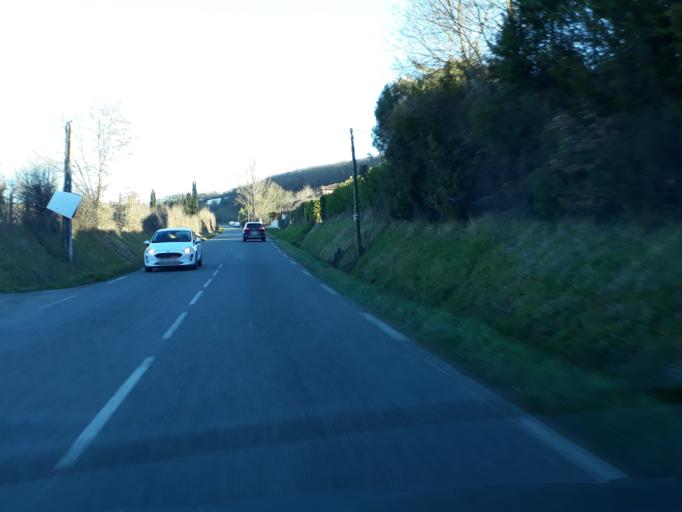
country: FR
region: Midi-Pyrenees
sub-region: Departement du Gers
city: Pavie
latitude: 43.6337
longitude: 0.6103
